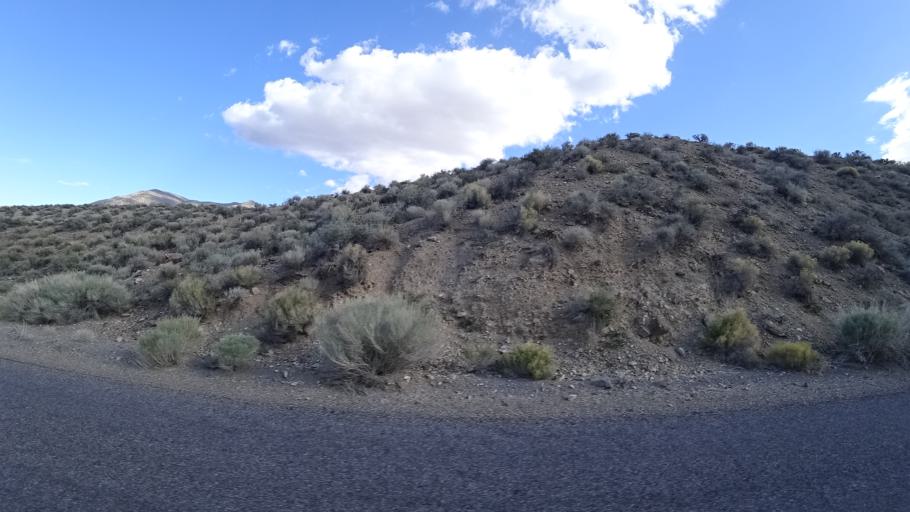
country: US
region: California
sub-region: San Bernardino County
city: Searles Valley
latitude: 36.3350
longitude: -117.1363
